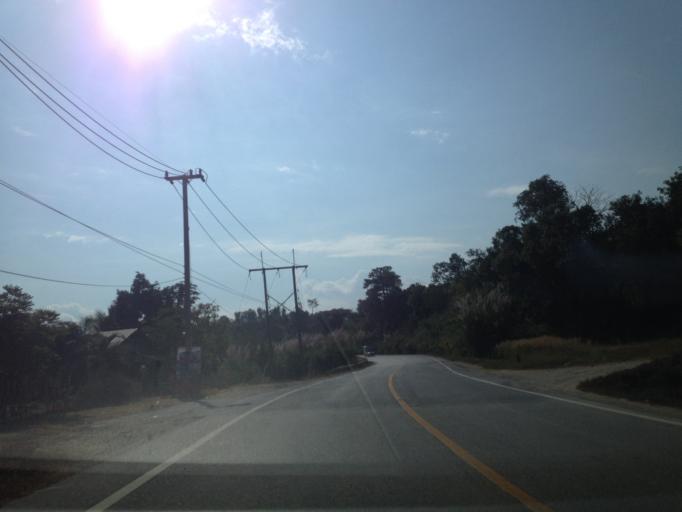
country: TH
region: Mae Hong Son
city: Pa Pae
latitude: 18.1647
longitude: 98.2325
